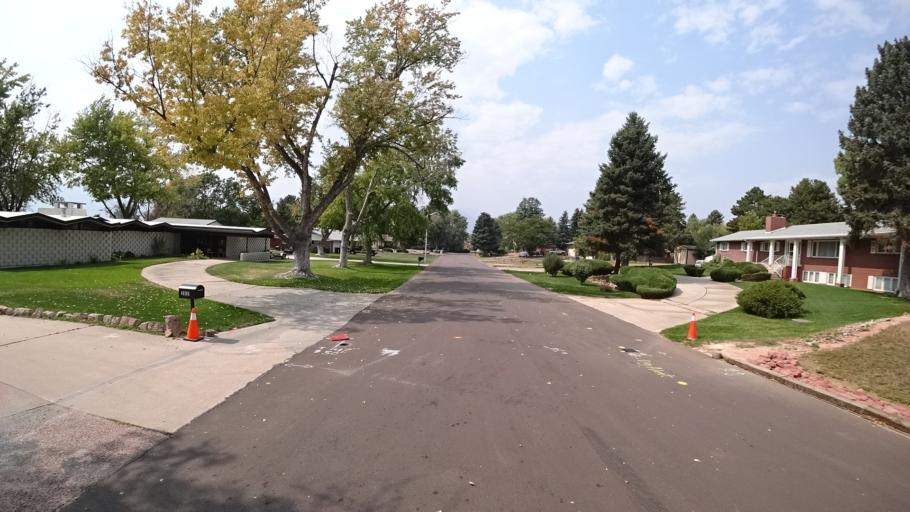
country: US
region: Colorado
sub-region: El Paso County
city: Colorado Springs
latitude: 38.8237
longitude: -104.7742
